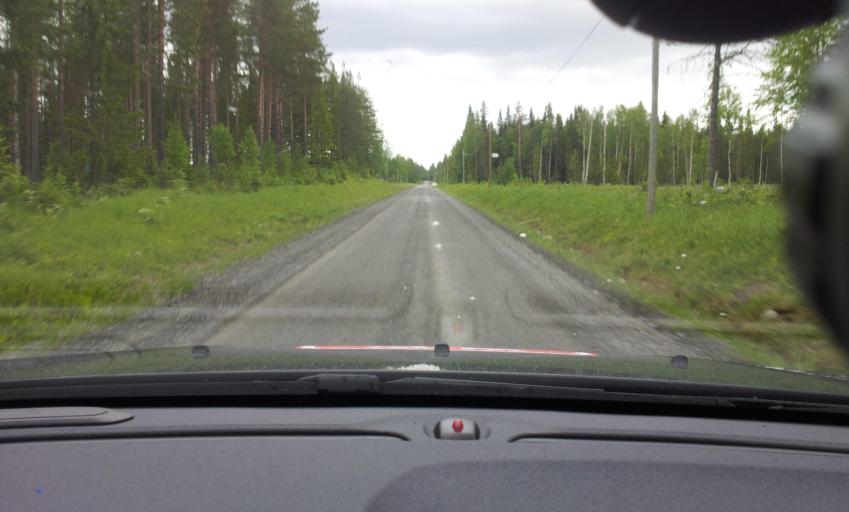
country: SE
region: Jaemtland
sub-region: OEstersunds Kommun
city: Brunflo
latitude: 63.1705
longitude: 14.9771
